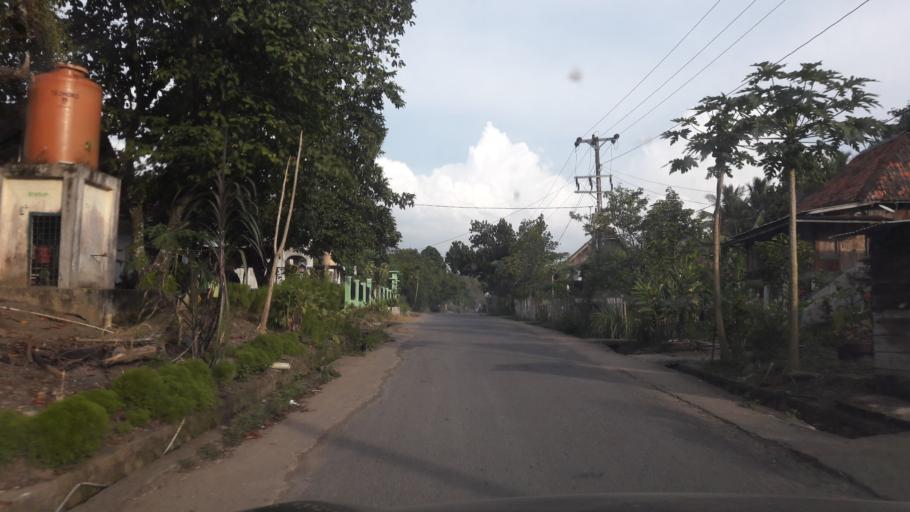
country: ID
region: South Sumatra
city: Gunungmenang
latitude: -3.2906
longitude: 104.0843
